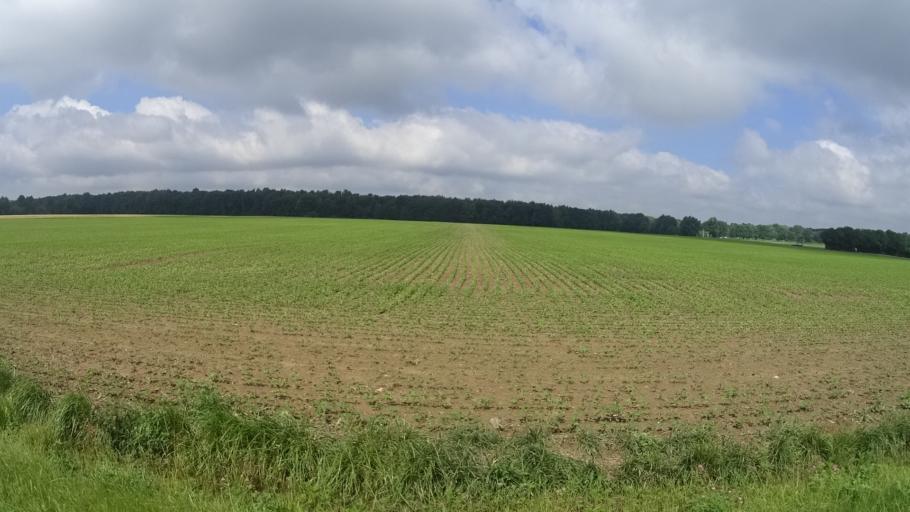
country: US
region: Ohio
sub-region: Huron County
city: Wakeman
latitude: 41.3039
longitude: -82.4133
